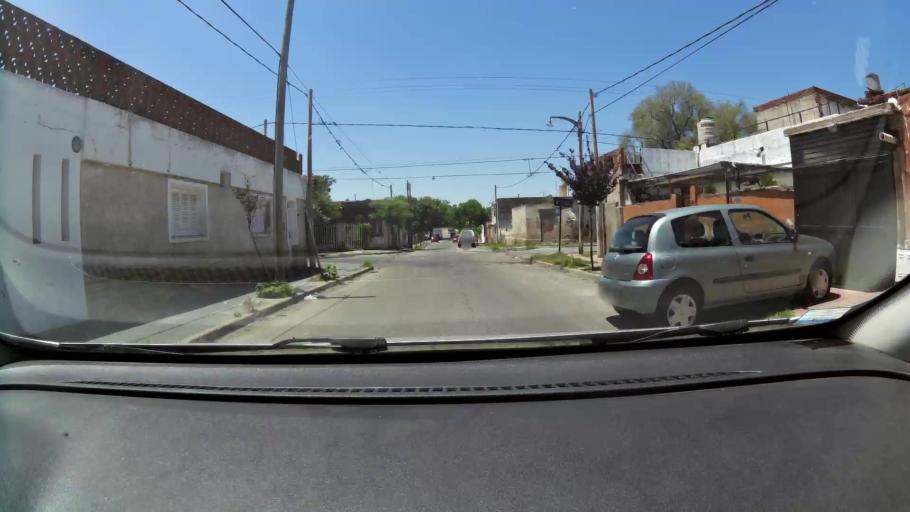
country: AR
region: Cordoba
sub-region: Departamento de Capital
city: Cordoba
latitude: -31.3976
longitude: -64.2072
